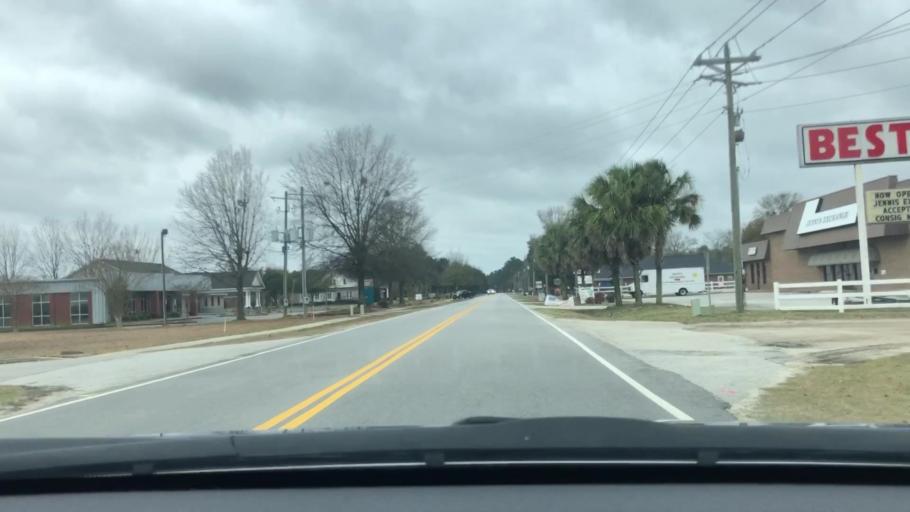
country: US
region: South Carolina
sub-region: Sumter County
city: Cherryvale
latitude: 33.9569
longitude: -80.3983
